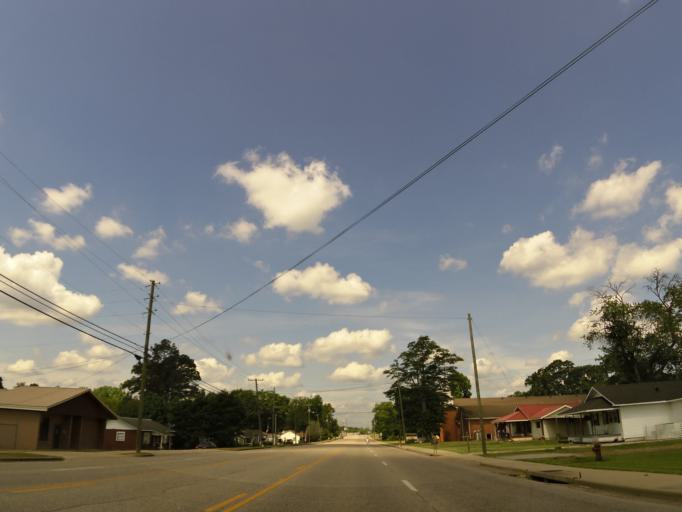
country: US
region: Alabama
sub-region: Marion County
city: Guin
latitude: 33.9665
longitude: -87.9029
